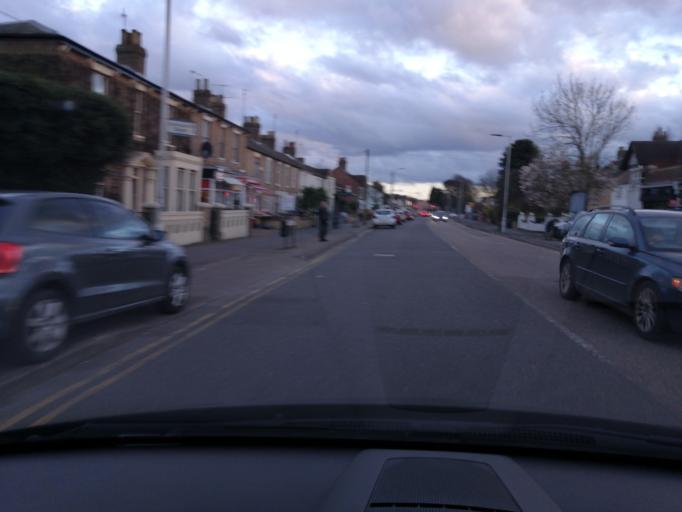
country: GB
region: England
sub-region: Peterborough
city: Peterborough
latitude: 52.5859
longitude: -0.2462
